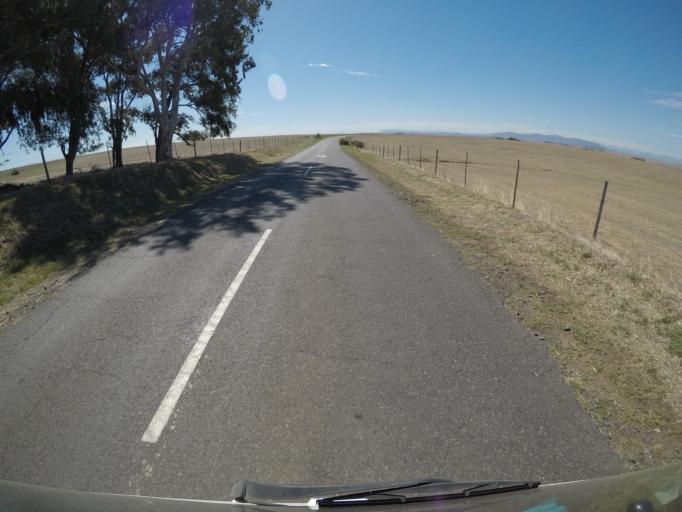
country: ZA
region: Western Cape
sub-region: City of Cape Town
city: Atlantis
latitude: -33.6927
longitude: 18.5933
